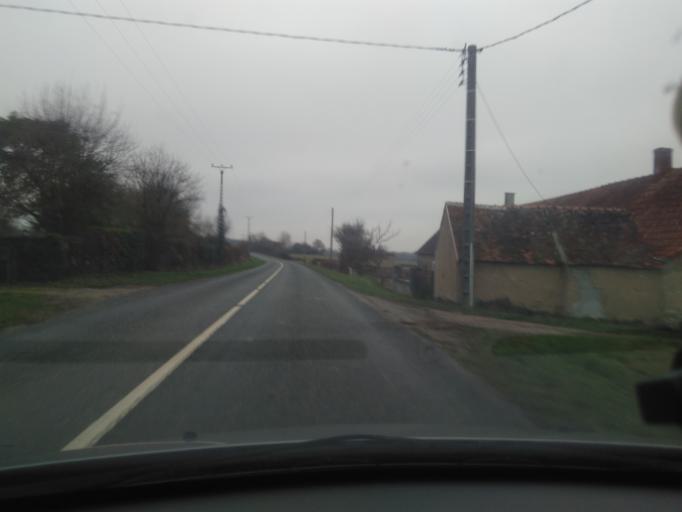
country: FR
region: Centre
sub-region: Departement du Cher
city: Chateaumeillant
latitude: 46.6331
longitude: 2.1310
